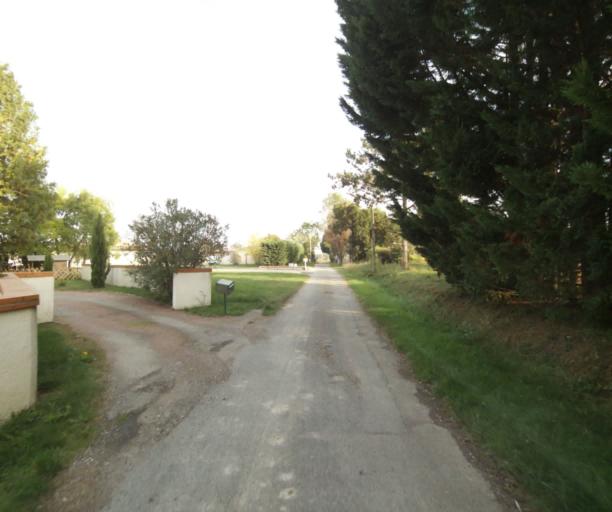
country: FR
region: Midi-Pyrenees
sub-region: Departement du Tarn-et-Garonne
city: Campsas
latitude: 43.8884
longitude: 1.3345
